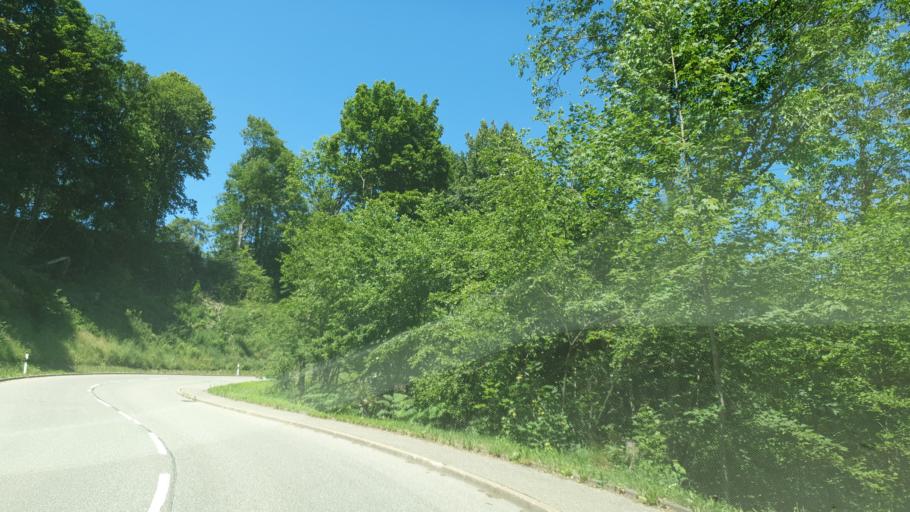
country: DE
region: Baden-Wuerttemberg
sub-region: Freiburg Region
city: Horben
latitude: 47.9425
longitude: 7.8610
